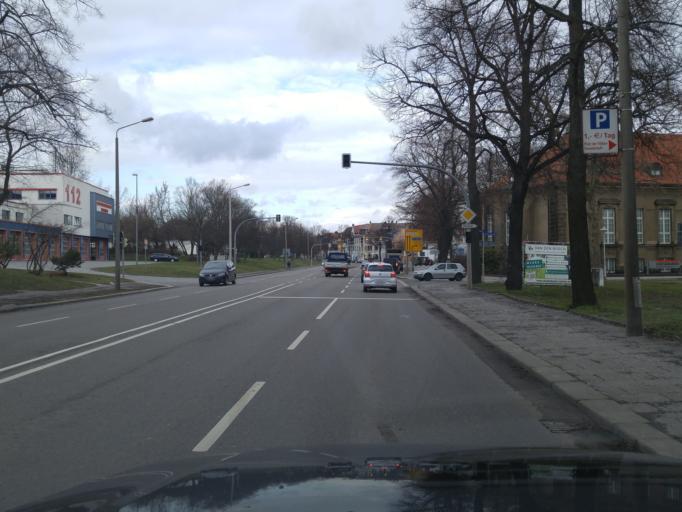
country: DE
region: Saxony
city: Zwickau
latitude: 50.7239
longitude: 12.4864
